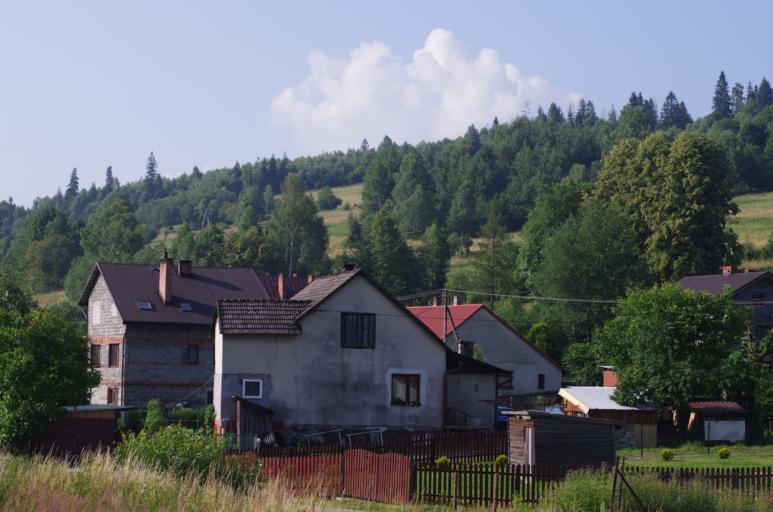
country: PL
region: Silesian Voivodeship
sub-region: Powiat zywiecki
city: Rajcza
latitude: 49.5256
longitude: 19.1070
